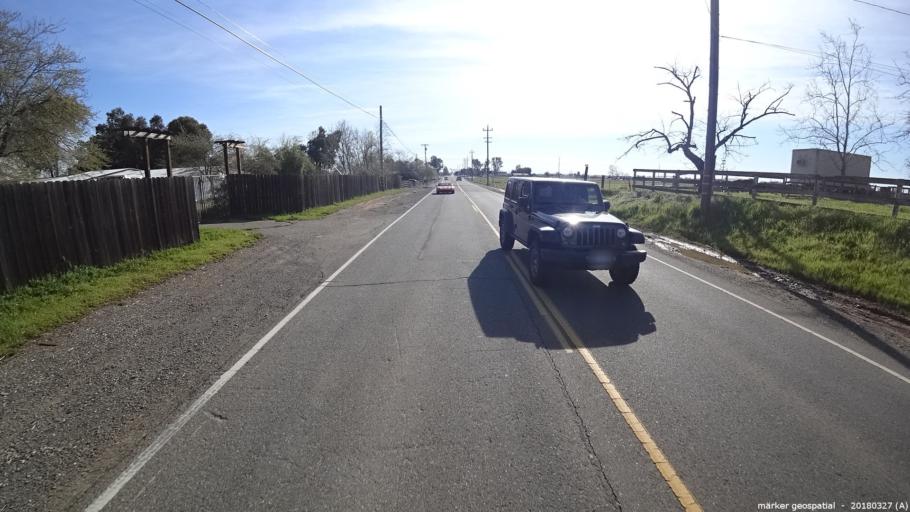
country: US
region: California
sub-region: Sacramento County
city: Vineyard
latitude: 38.4963
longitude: -121.3386
